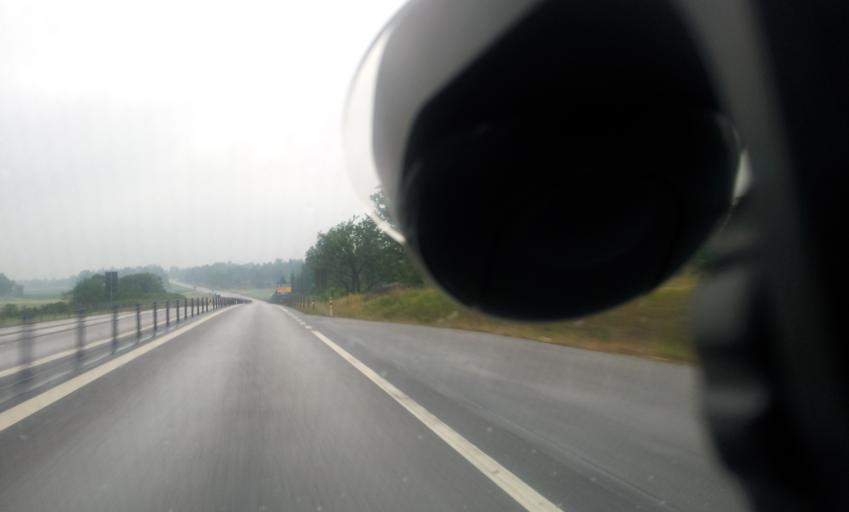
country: SE
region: Kalmar
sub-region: Vasterviks Kommun
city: Gamleby
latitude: 57.8745
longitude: 16.4041
